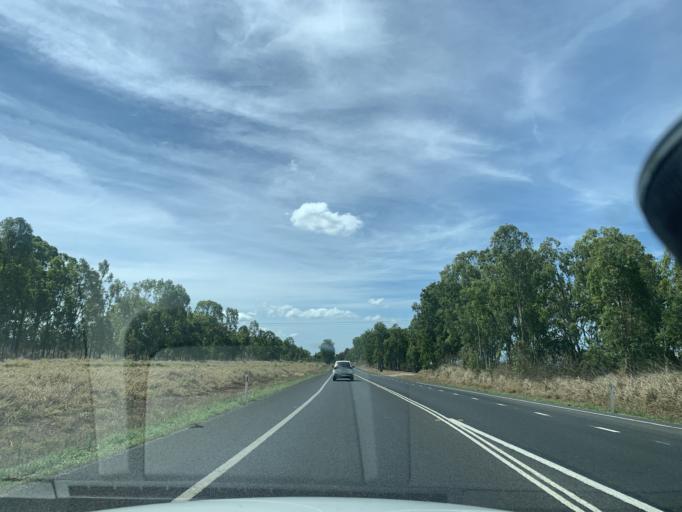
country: AU
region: Queensland
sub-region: Tablelands
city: Tolga
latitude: -17.2015
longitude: 145.4750
